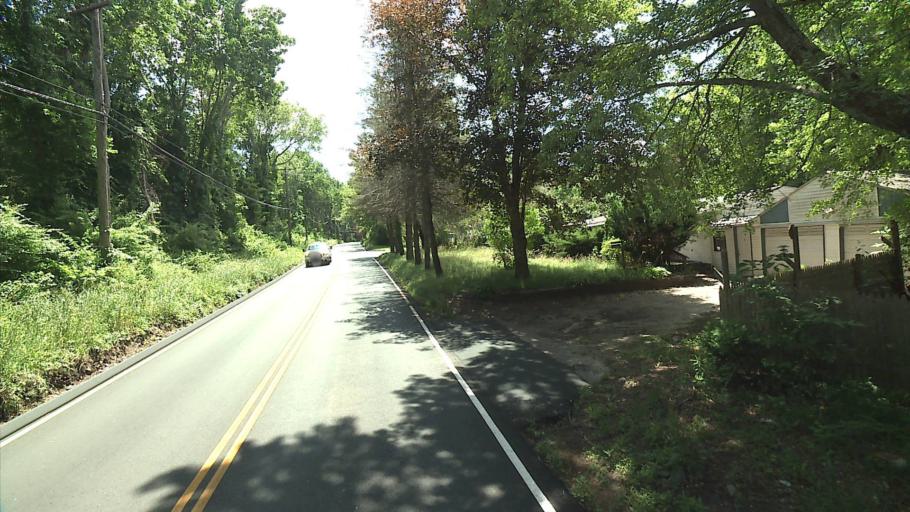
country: US
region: Connecticut
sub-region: New London County
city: Jewett City
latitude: 41.5793
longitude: -71.8982
